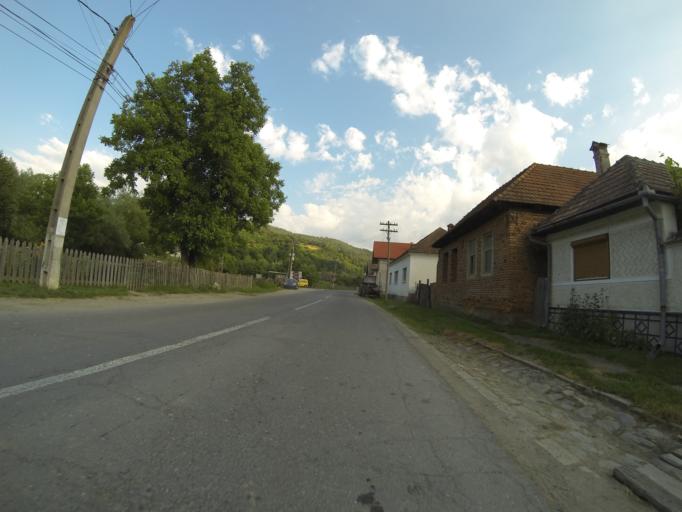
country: RO
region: Brasov
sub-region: Comuna Sinca Noua
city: Sinca Noua
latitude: 45.7057
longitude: 25.2456
